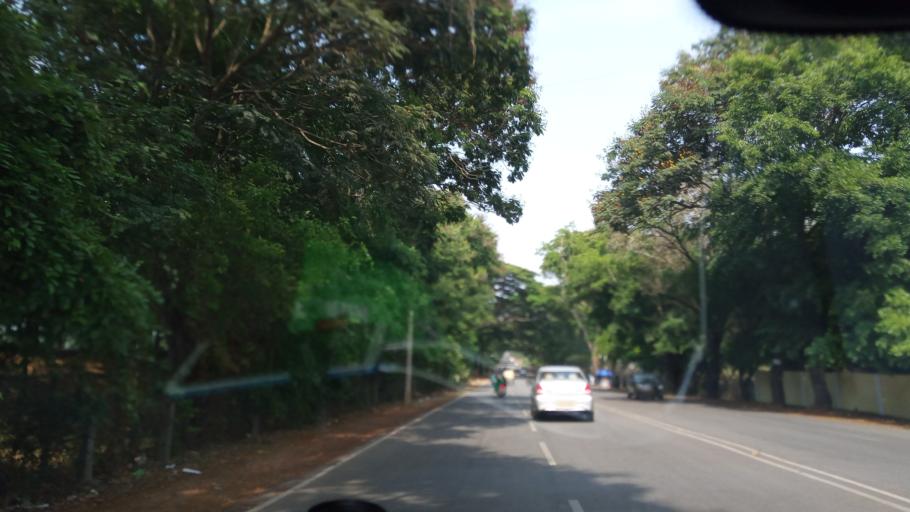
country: IN
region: Karnataka
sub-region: Mysore
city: Mysore
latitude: 12.3063
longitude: 76.6280
